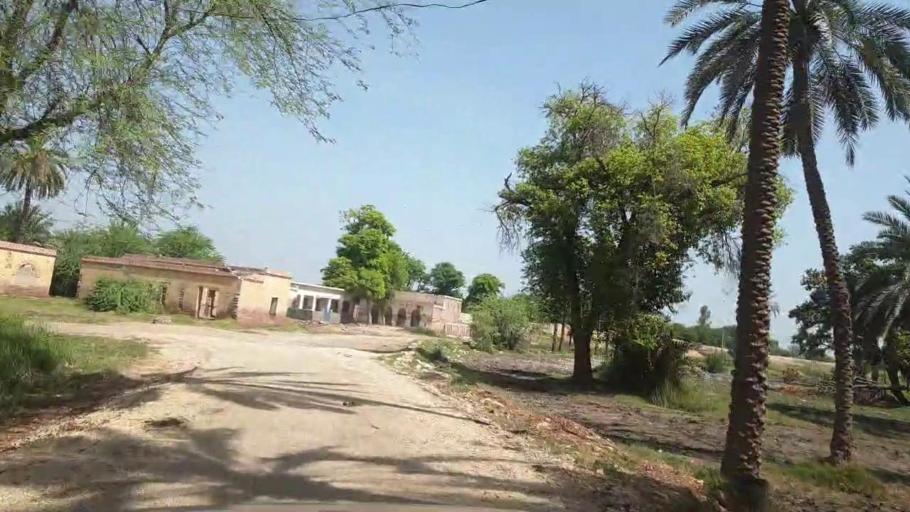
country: PK
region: Sindh
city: Rohri
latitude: 27.6961
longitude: 68.9464
